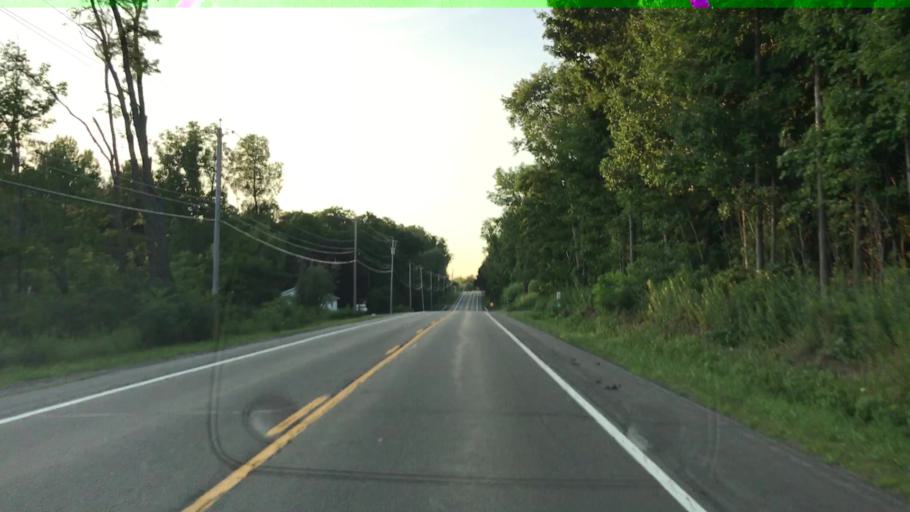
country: US
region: New York
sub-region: Chautauqua County
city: Mayville
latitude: 42.2541
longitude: -79.4661
